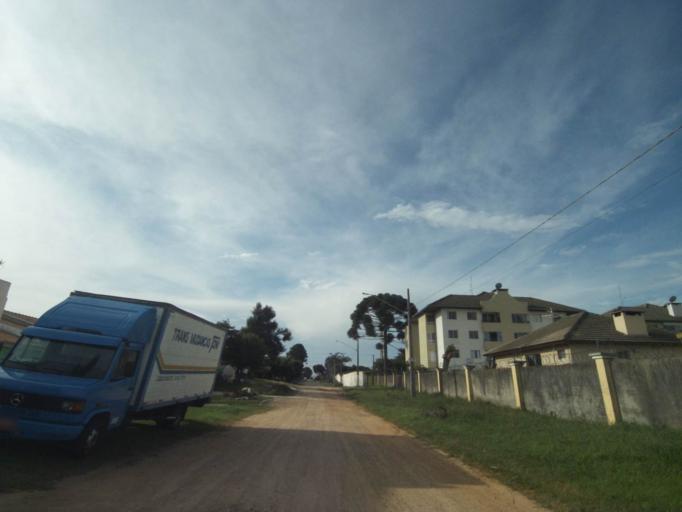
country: BR
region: Parana
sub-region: Pinhais
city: Pinhais
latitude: -25.4574
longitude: -49.2217
